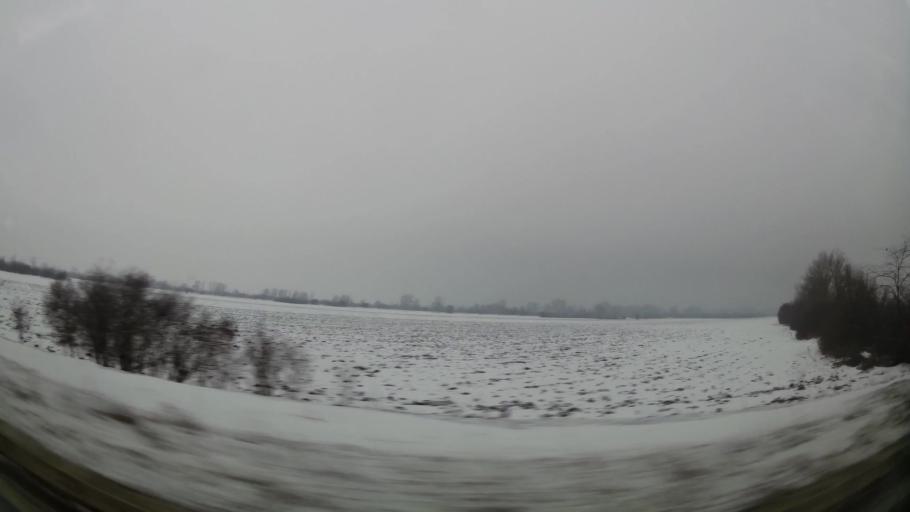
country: RS
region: Central Serbia
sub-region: Belgrade
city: Cukarica
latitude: 44.7528
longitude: 20.3793
